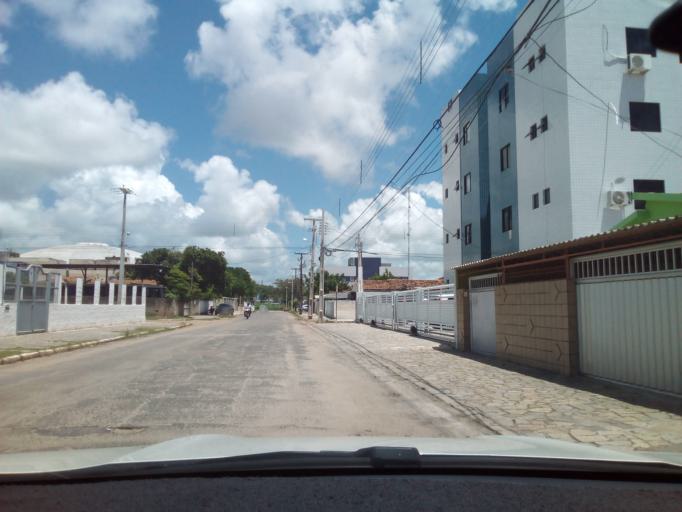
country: BR
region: Paraiba
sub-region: Joao Pessoa
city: Joao Pessoa
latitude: -7.1669
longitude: -34.8696
